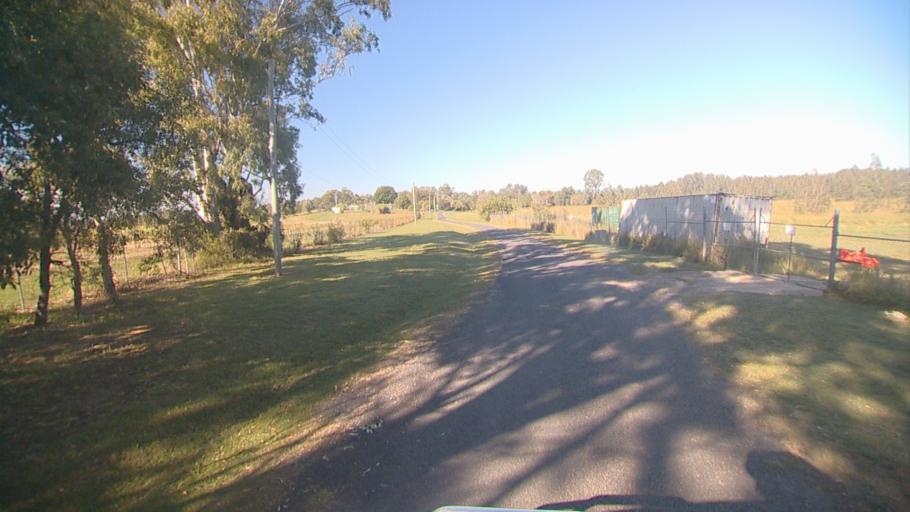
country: AU
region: Queensland
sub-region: Gold Coast
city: Yatala
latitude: -27.6914
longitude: 153.2797
